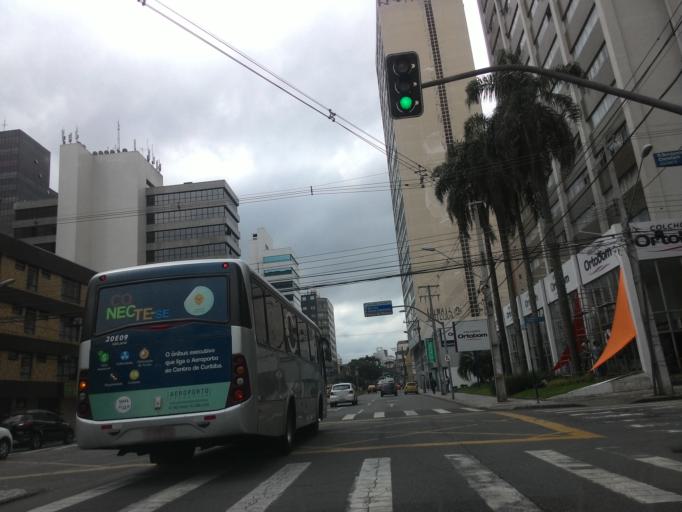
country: BR
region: Parana
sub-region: Curitiba
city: Curitiba
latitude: -25.4298
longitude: -49.2628
